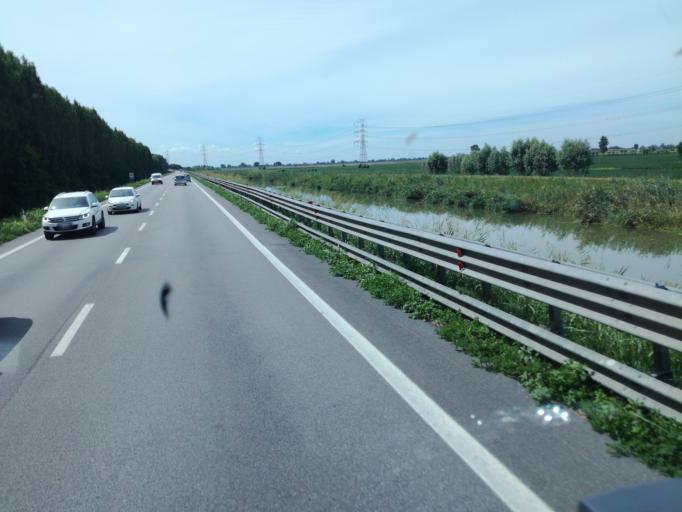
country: IT
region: Veneto
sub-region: Provincia di Padova
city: Codevigo
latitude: 45.2705
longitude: 12.1288
